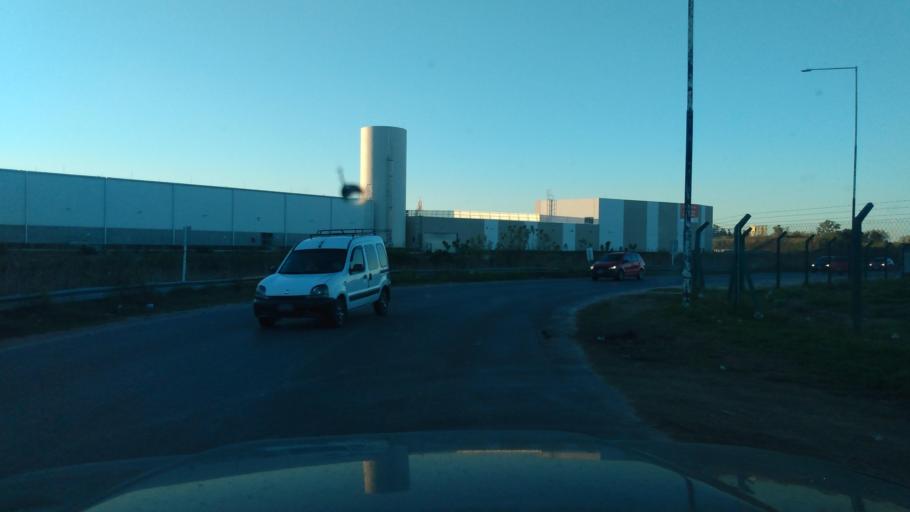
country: AR
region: Buenos Aires
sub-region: Partido de Merlo
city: Merlo
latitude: -34.6317
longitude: -58.7266
